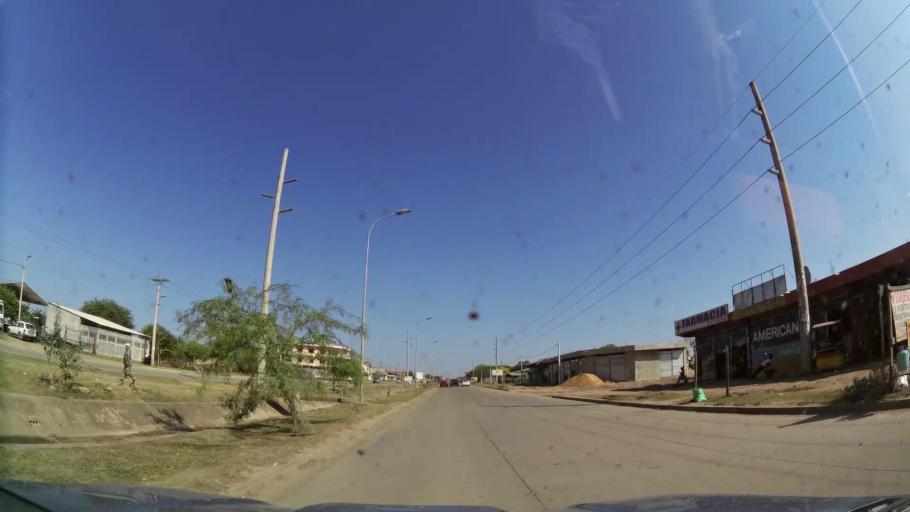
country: BO
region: Santa Cruz
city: Cotoca
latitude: -17.7821
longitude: -63.1081
